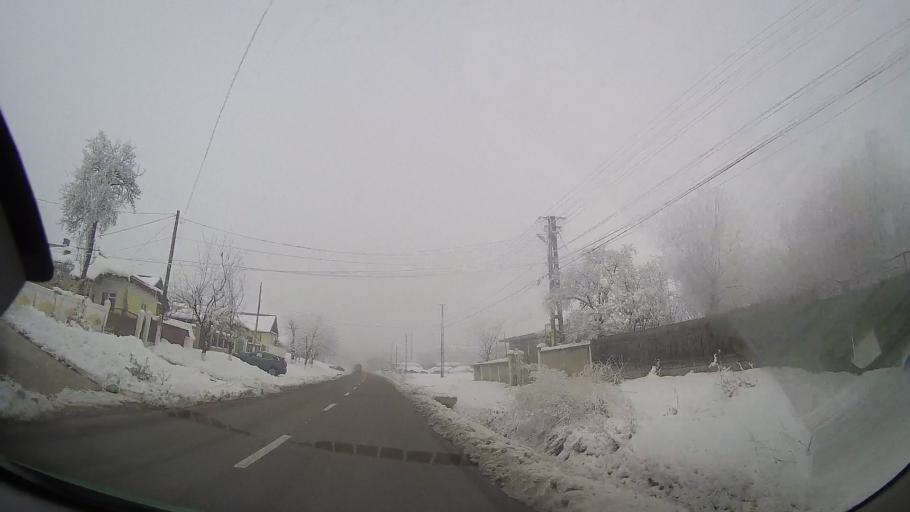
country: RO
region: Iasi
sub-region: Comuna Halaucesti
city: Halaucesti
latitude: 47.0979
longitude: 26.8184
